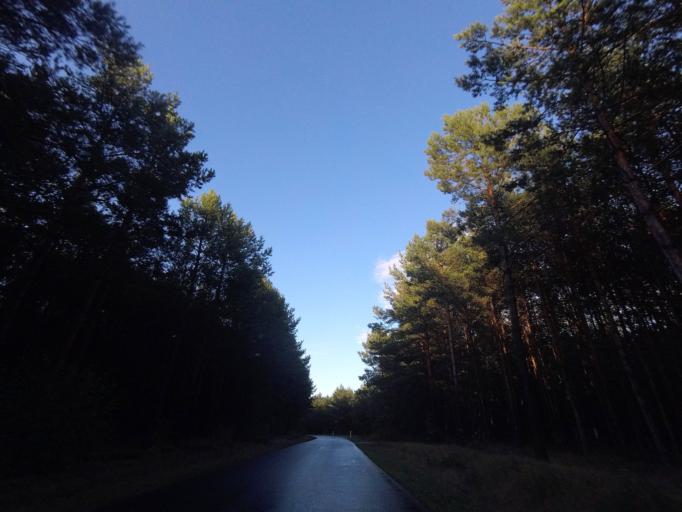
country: DE
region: Brandenburg
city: Treuenbrietzen
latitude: 52.0469
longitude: 12.8701
